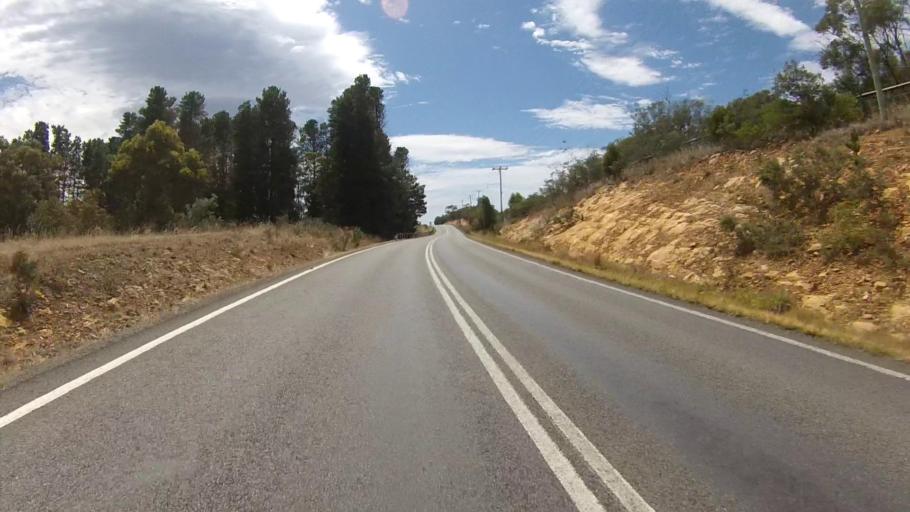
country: AU
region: Tasmania
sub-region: Brighton
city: Old Beach
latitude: -42.6715
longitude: 147.3629
